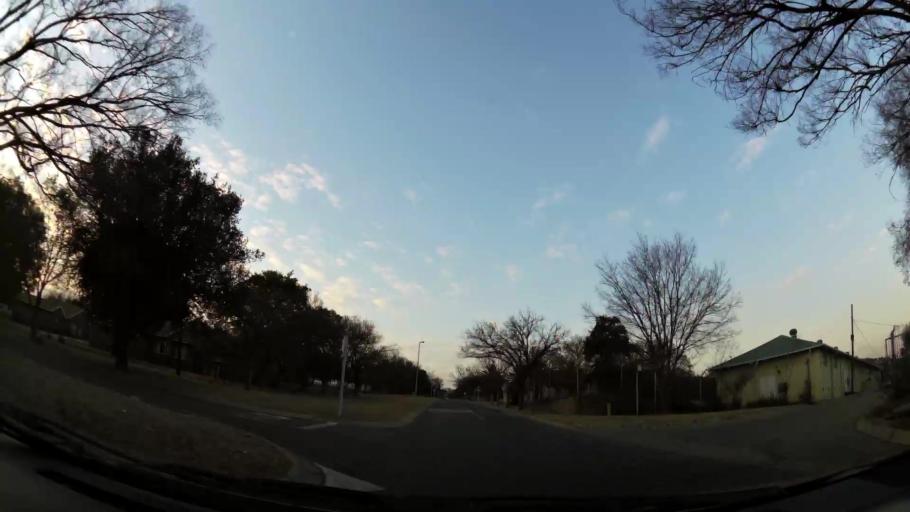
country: ZA
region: Gauteng
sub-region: City of Johannesburg Metropolitan Municipality
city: Diepsloot
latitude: -26.0065
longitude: 28.0453
